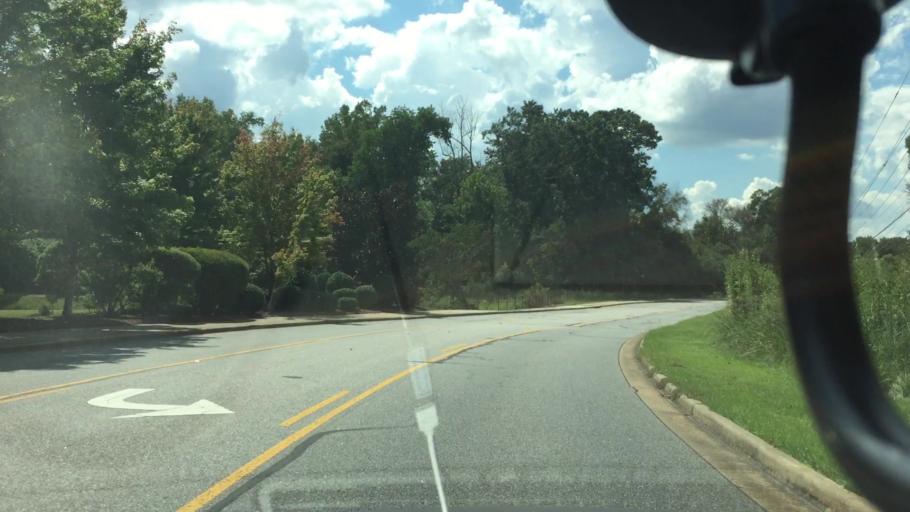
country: US
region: Alabama
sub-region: Lee County
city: Auburn
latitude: 32.5728
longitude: -85.5061
